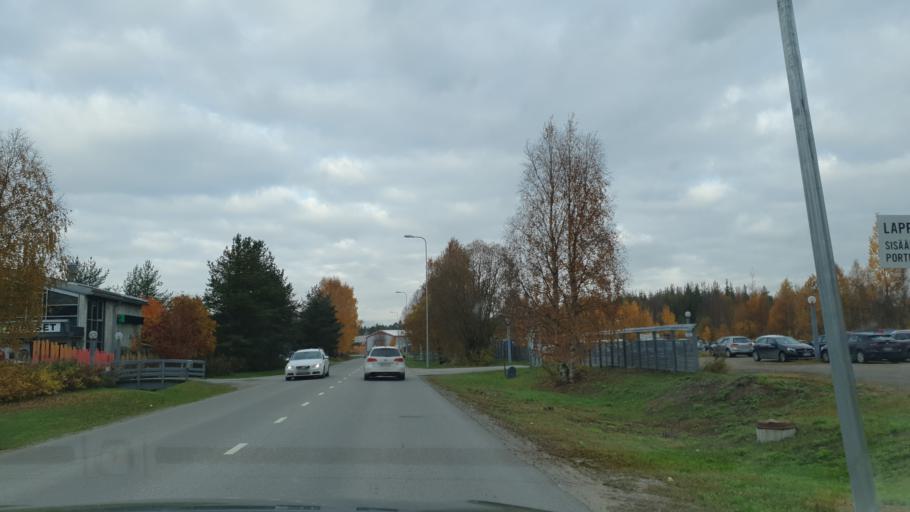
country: FI
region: Lapland
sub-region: Rovaniemi
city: Rovaniemi
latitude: 66.4939
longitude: 25.6756
